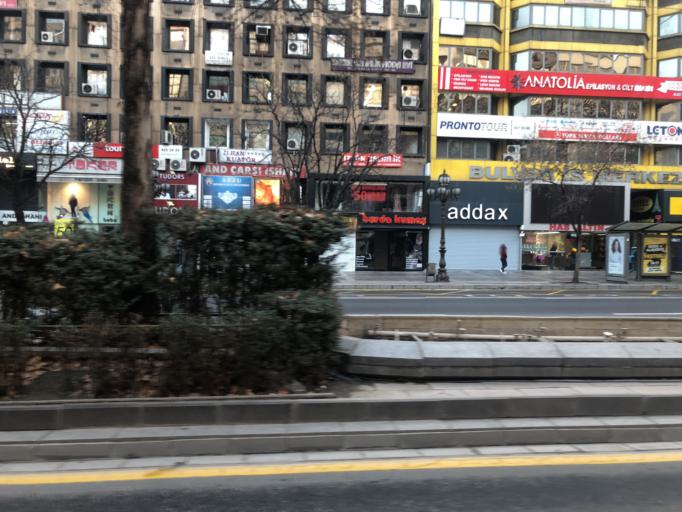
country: TR
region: Ankara
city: Ankara
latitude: 39.9237
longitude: 32.8544
